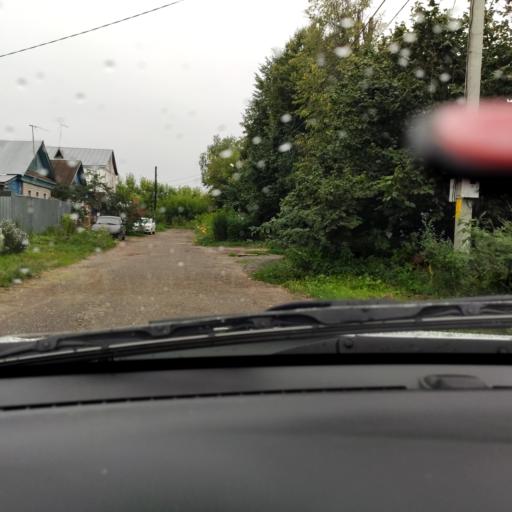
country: RU
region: Tatarstan
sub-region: Gorod Kazan'
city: Kazan
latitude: 55.8428
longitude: 49.1973
